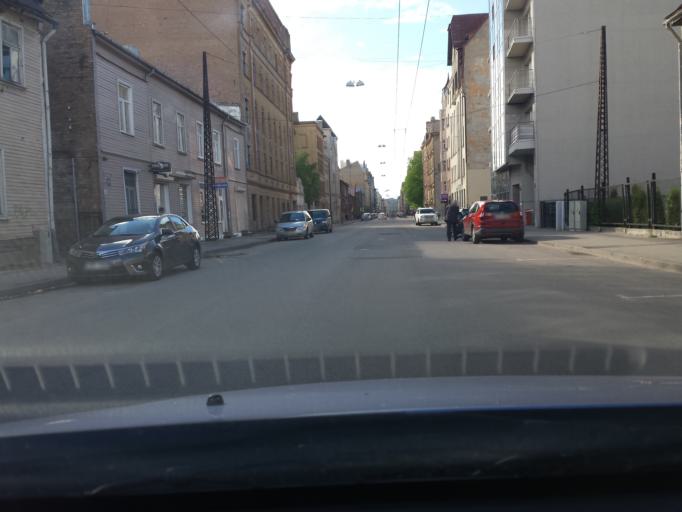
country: LV
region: Riga
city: Riga
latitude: 56.9535
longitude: 24.1410
